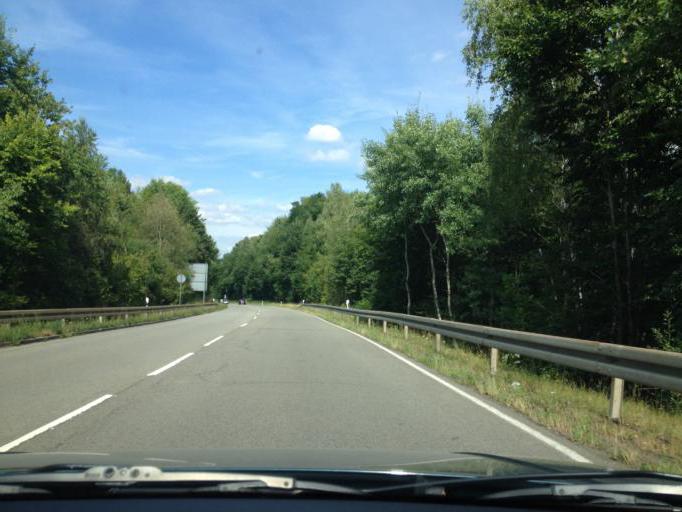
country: DE
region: Saarland
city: Neunkirchen
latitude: 49.3346
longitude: 7.1686
